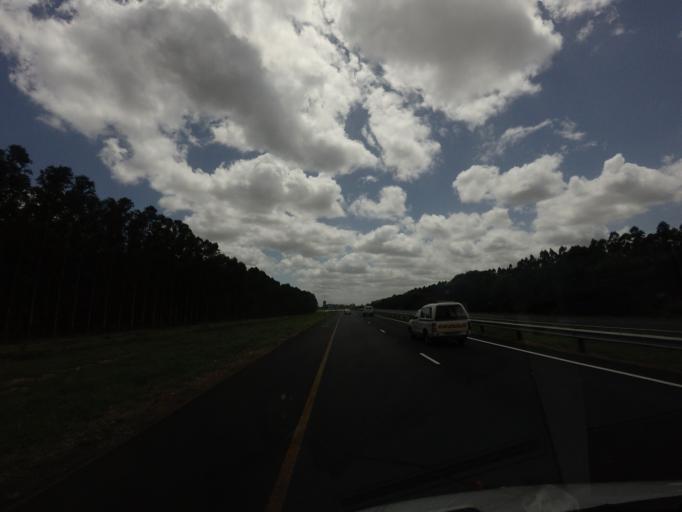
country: ZA
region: KwaZulu-Natal
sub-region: uThungulu District Municipality
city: KwaMbonambi
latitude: -28.5306
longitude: 32.1352
